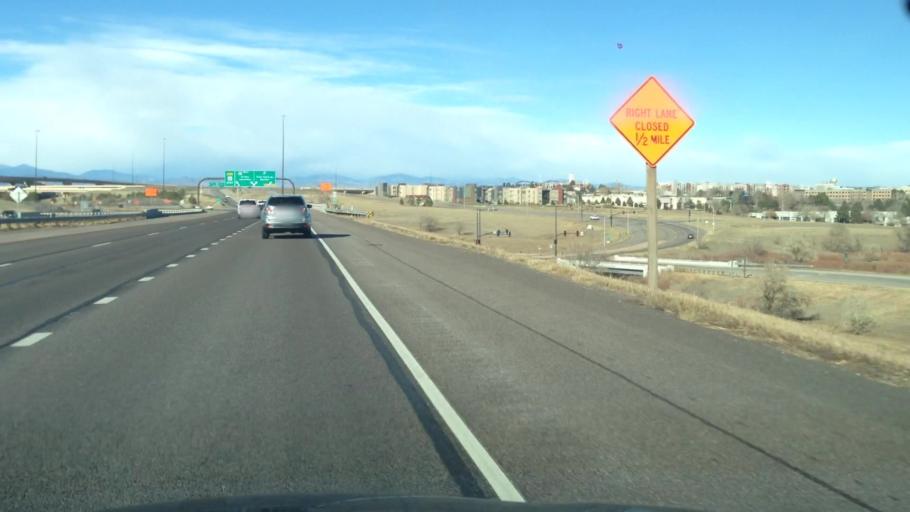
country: US
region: Colorado
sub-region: Douglas County
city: Meridian
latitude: 39.5534
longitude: -104.8598
